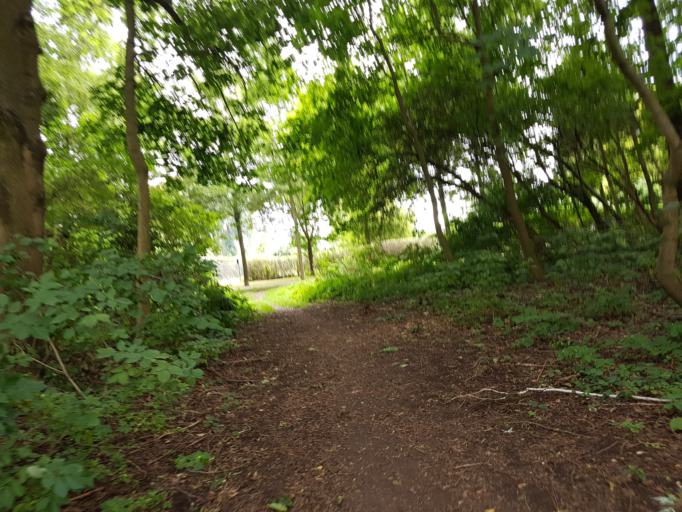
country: DE
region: Brandenburg
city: Finsterwalde
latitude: 51.6283
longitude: 13.6928
